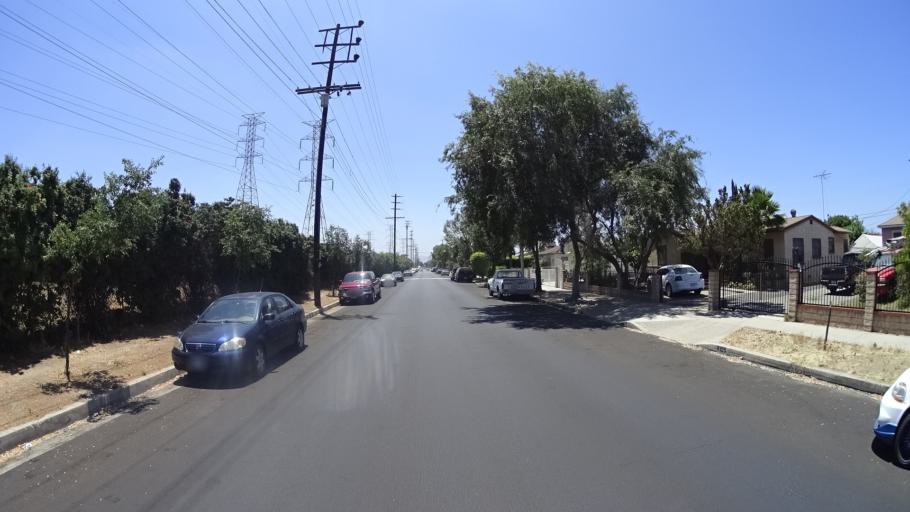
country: US
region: California
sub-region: Los Angeles County
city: San Fernando
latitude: 34.2359
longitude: -118.4312
